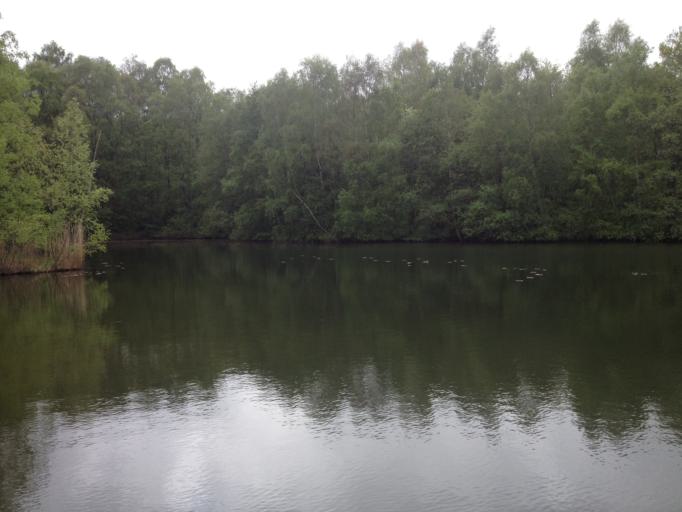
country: SE
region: Skane
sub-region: Lunds Kommun
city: Genarp
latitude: 55.6973
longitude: 13.3708
